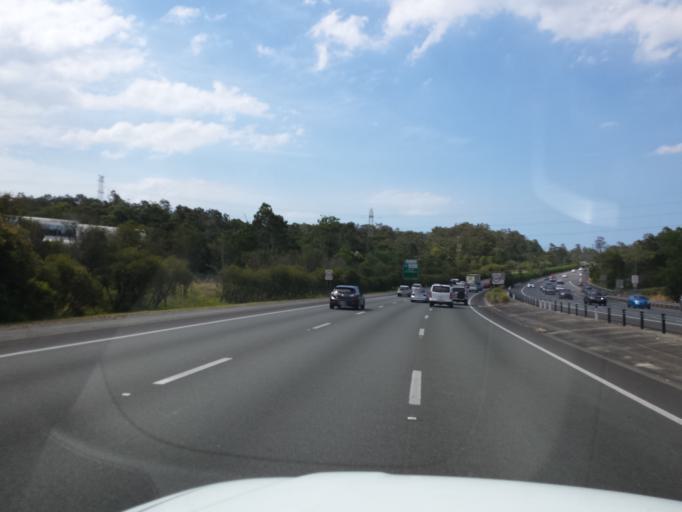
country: AU
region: Queensland
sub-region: Gold Coast
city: Nerang
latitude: -27.9803
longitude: 153.3422
